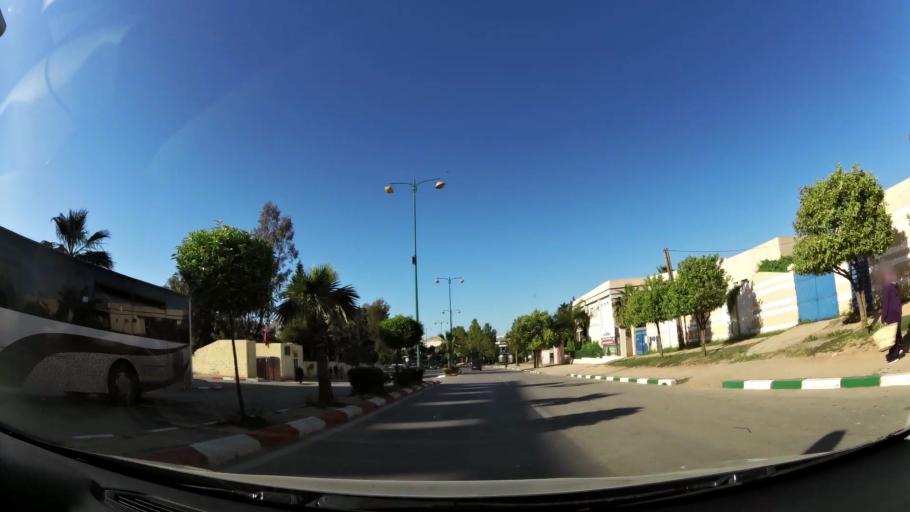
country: MA
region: Meknes-Tafilalet
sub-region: Meknes
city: Meknes
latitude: 33.8704
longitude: -5.5762
